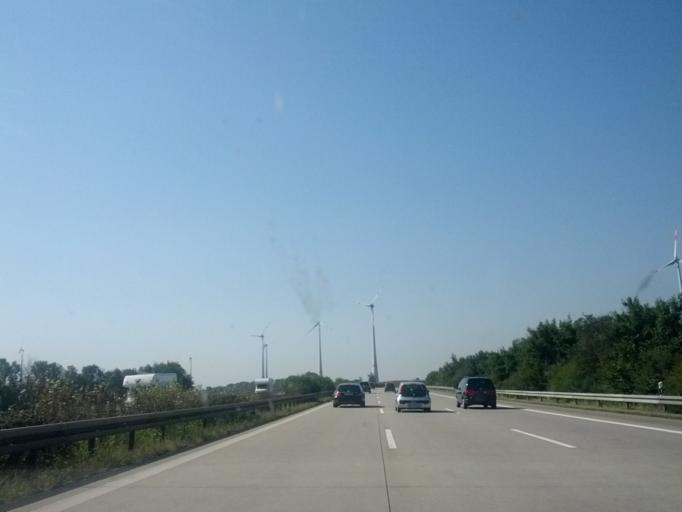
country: DE
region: Brandenburg
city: Borkheide
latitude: 52.1804
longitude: 12.8405
